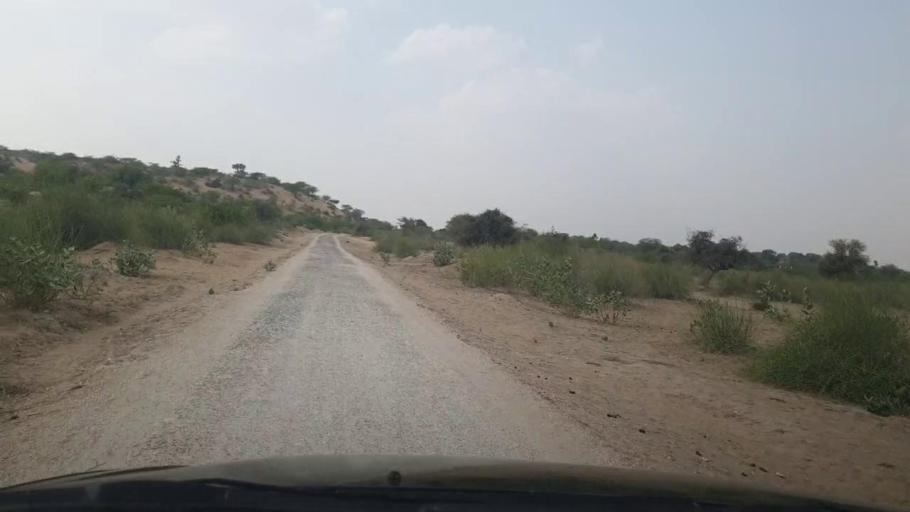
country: PK
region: Sindh
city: Islamkot
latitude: 24.9520
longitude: 70.6382
